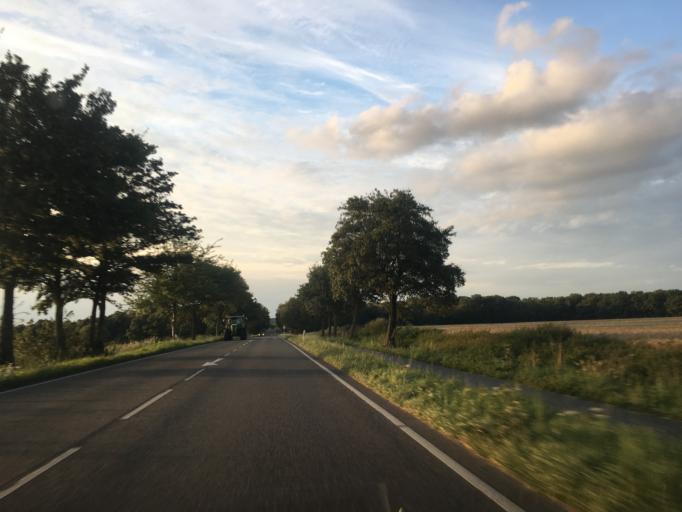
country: DE
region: North Rhine-Westphalia
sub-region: Regierungsbezirk Koln
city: Linnich
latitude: 51.0164
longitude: 6.2758
